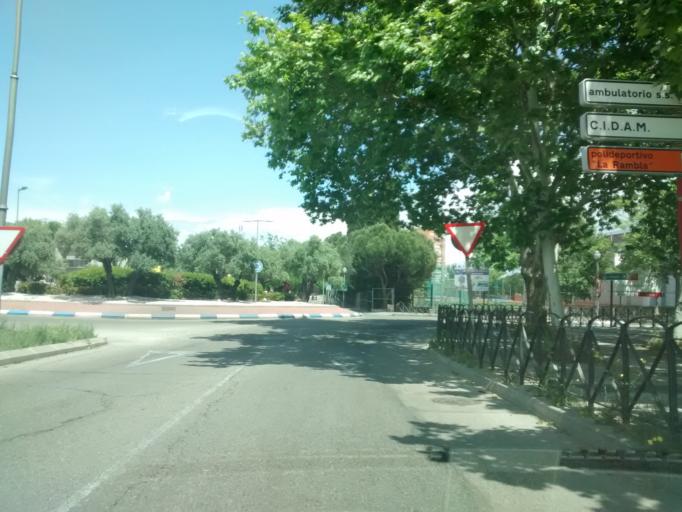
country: ES
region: Madrid
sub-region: Provincia de Madrid
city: San Fernando de Henares
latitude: 40.4299
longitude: -3.5456
